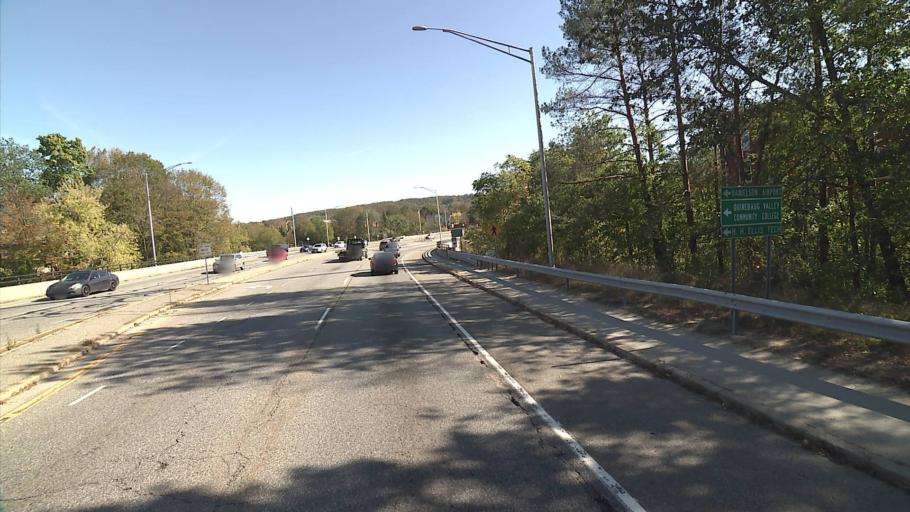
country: US
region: Connecticut
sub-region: Windham County
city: Danielson
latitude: 41.8018
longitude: -71.8888
